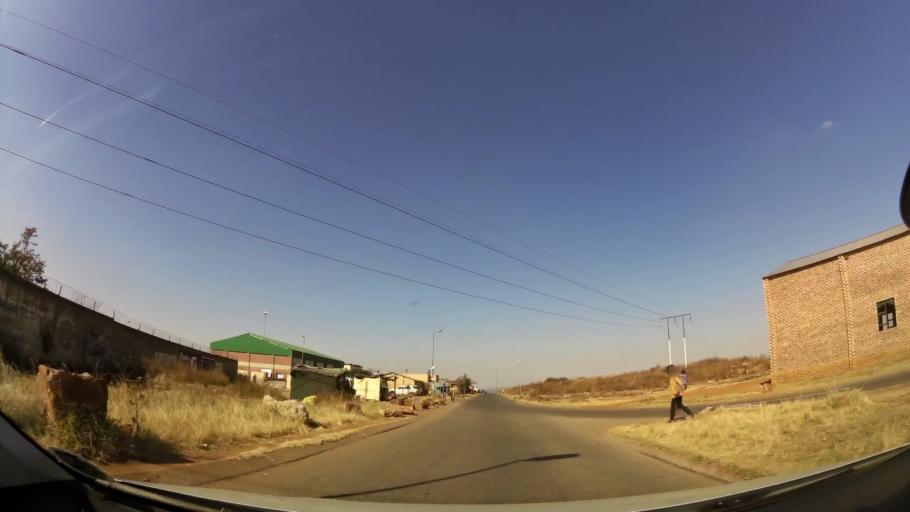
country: ZA
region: Gauteng
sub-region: City of Johannesburg Metropolitan Municipality
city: Soweto
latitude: -26.2814
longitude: 27.8633
